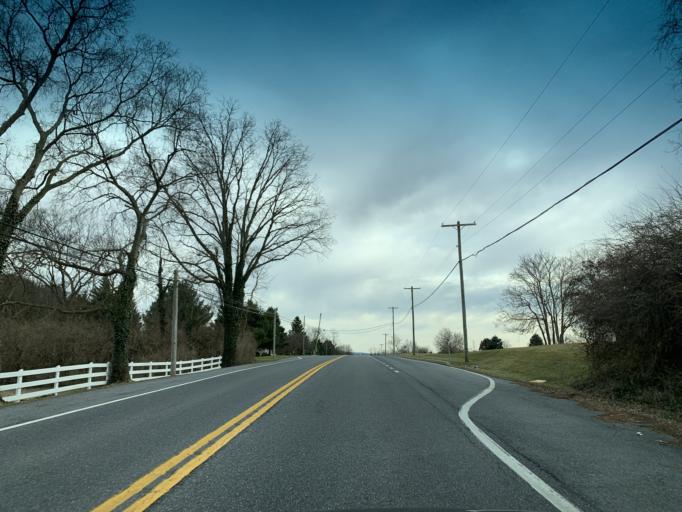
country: US
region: Maryland
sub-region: Washington County
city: Robinwood
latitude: 39.5767
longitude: -77.6922
